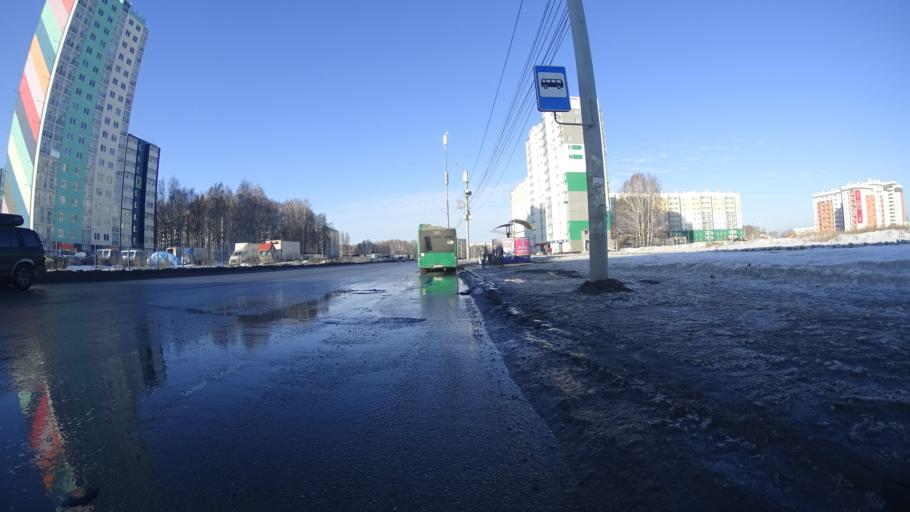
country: RU
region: Chelyabinsk
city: Roshchino
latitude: 55.2106
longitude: 61.2843
